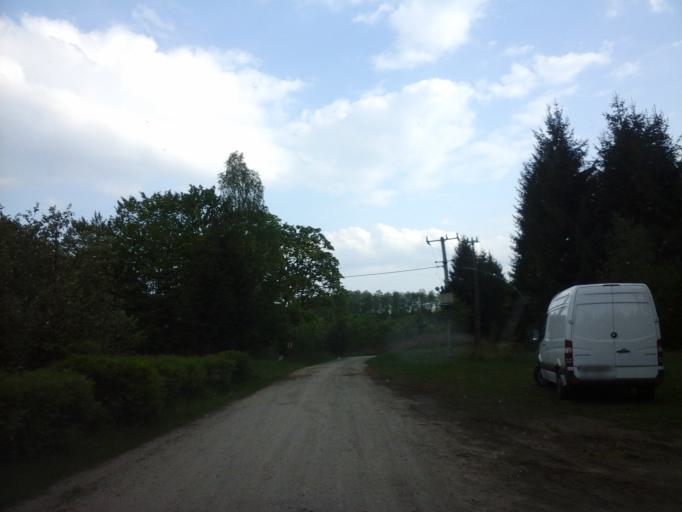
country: PL
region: West Pomeranian Voivodeship
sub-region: Powiat choszczenski
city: Pelczyce
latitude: 52.9469
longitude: 15.3470
